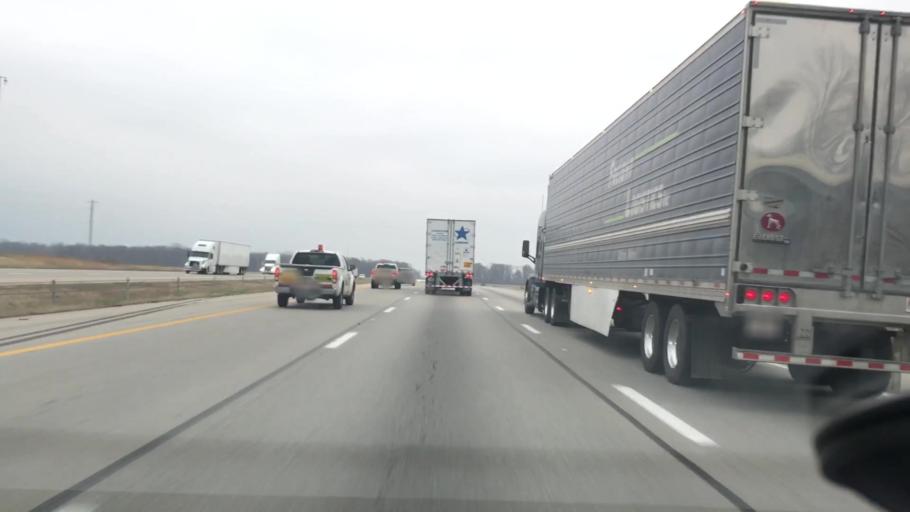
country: US
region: Ohio
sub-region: Clark County
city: Lisbon
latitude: 39.9347
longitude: -83.6455
